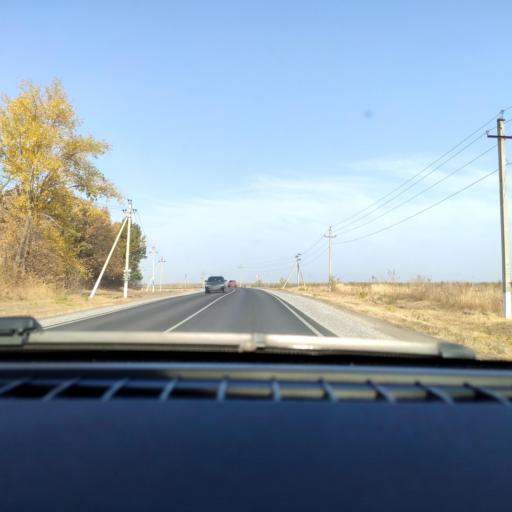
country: RU
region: Voronezj
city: Novaya Usman'
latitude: 51.6861
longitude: 39.3969
